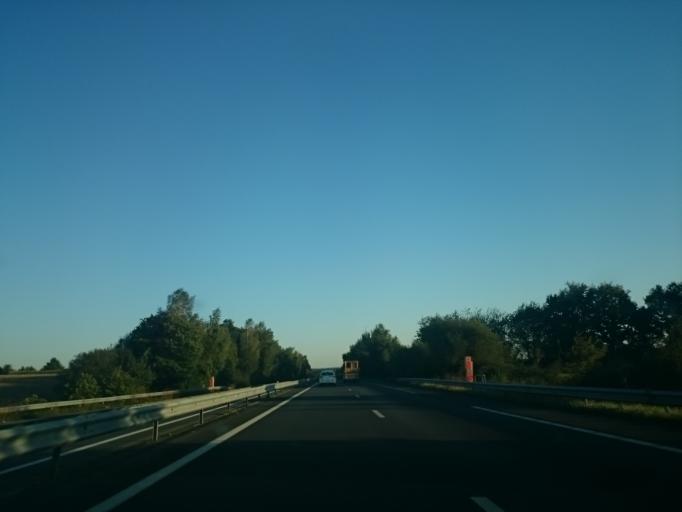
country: FR
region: Pays de la Loire
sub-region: Departement de la Loire-Atlantique
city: Derval
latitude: 47.6718
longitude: -1.6883
